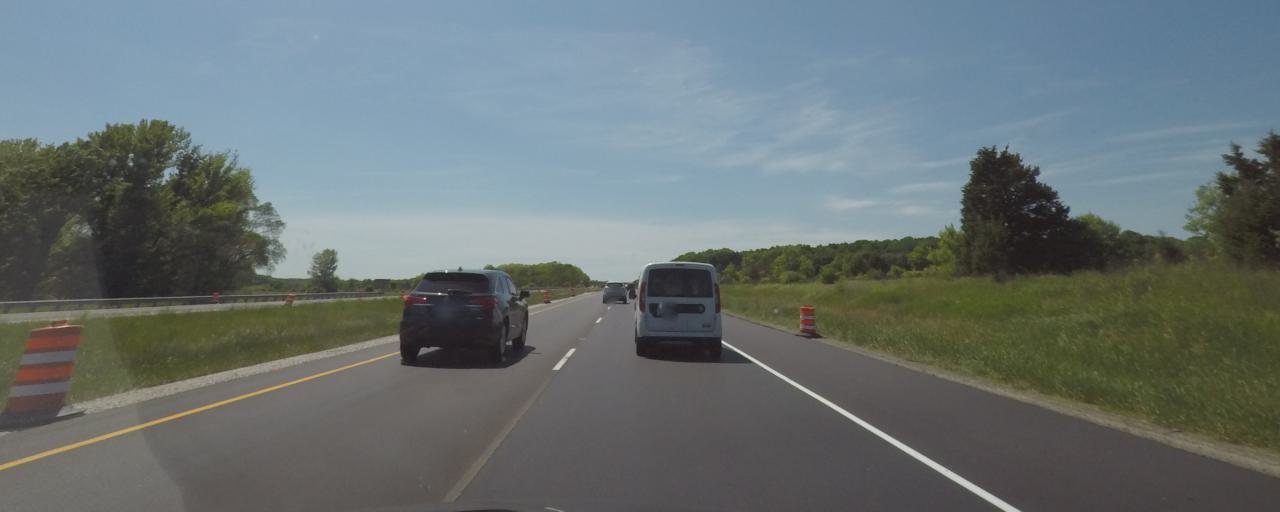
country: US
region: Wisconsin
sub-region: Jefferson County
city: Lake Mills
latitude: 43.1111
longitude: -88.9728
